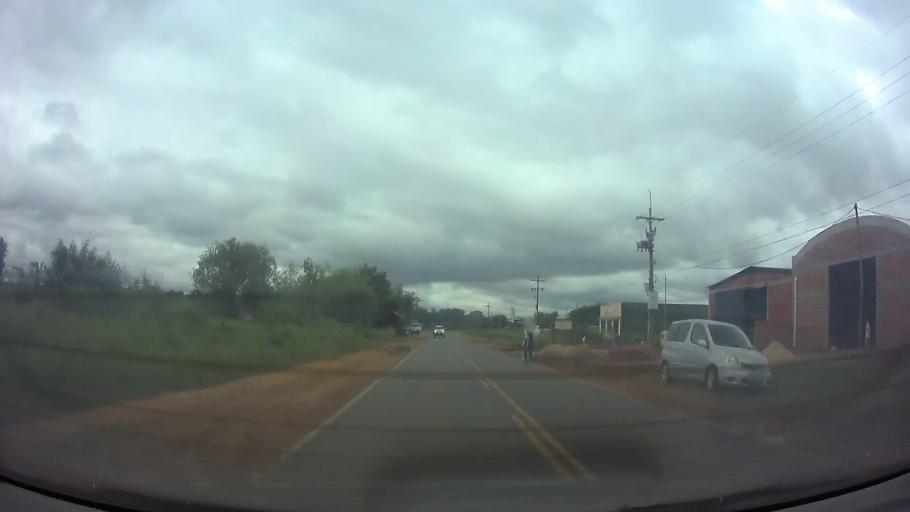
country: PY
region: Central
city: Guarambare
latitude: -25.4996
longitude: -57.4802
